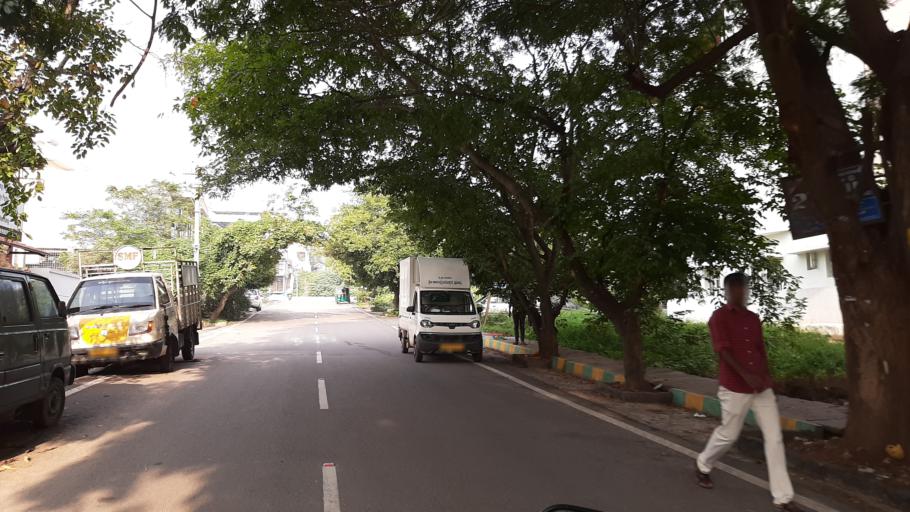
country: IN
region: Karnataka
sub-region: Bangalore Urban
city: Bangalore
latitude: 12.9692
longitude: 77.5133
